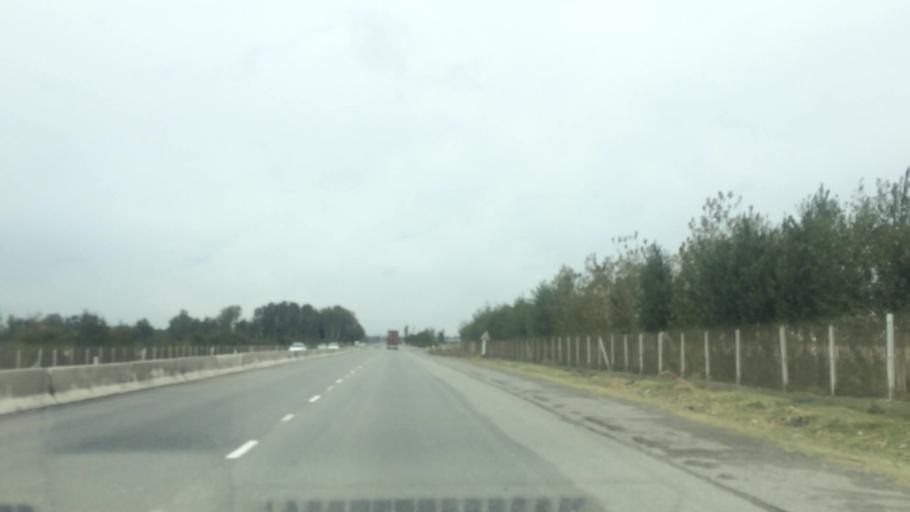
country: UZ
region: Samarqand
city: Bulung'ur
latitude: 39.7817
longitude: 67.2993
